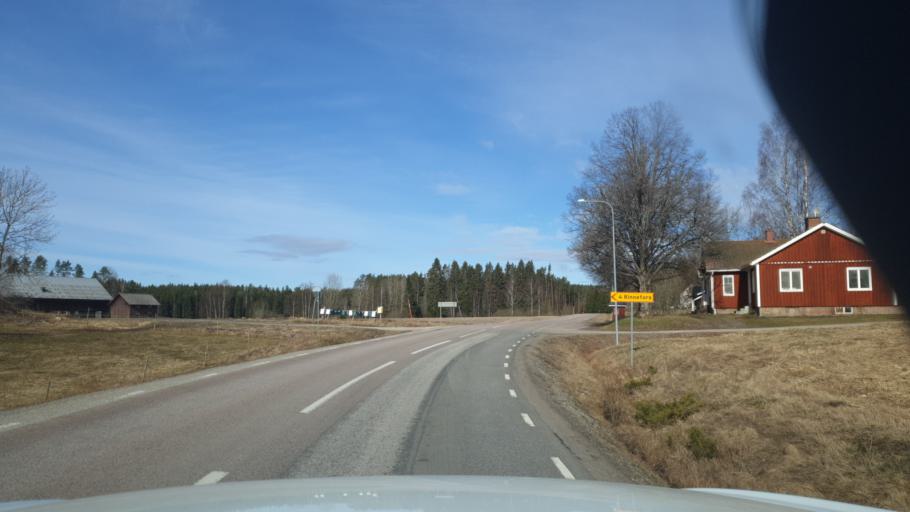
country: SE
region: Vaermland
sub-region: Sunne Kommun
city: Sunne
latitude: 59.6637
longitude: 13.0041
